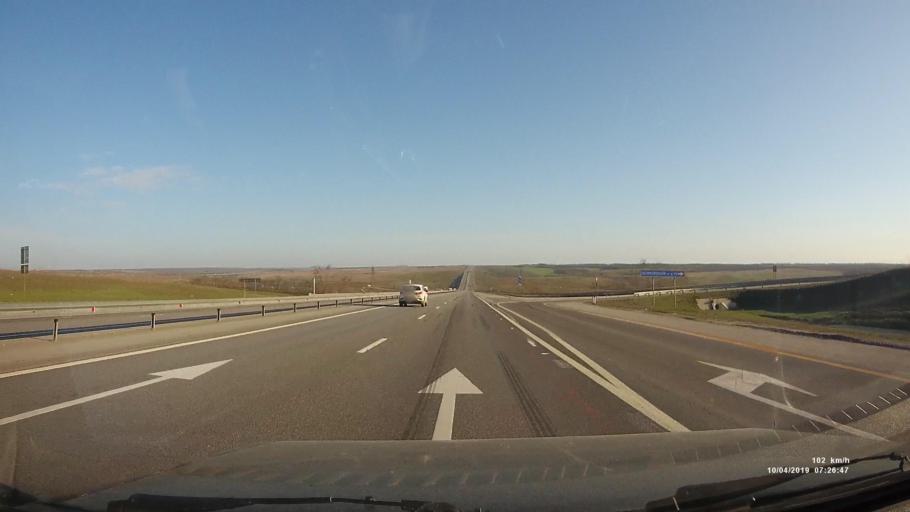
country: RU
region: Rostov
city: Gornyy
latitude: 47.9142
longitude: 40.2186
